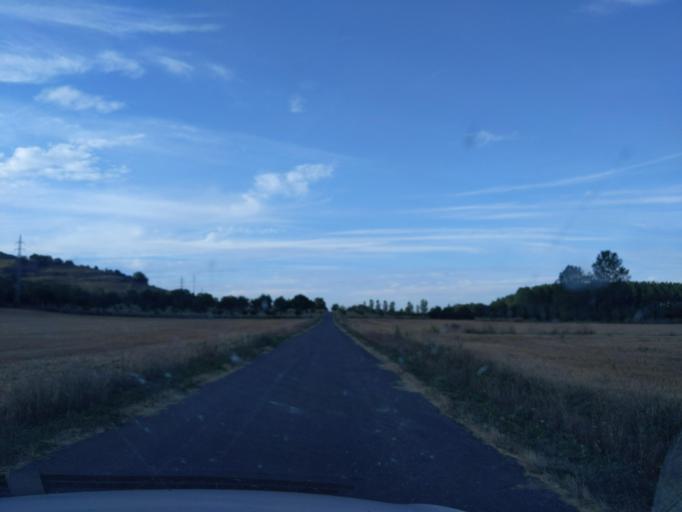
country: ES
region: La Rioja
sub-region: Provincia de La Rioja
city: Santurdejo
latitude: 42.3777
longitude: -2.9853
